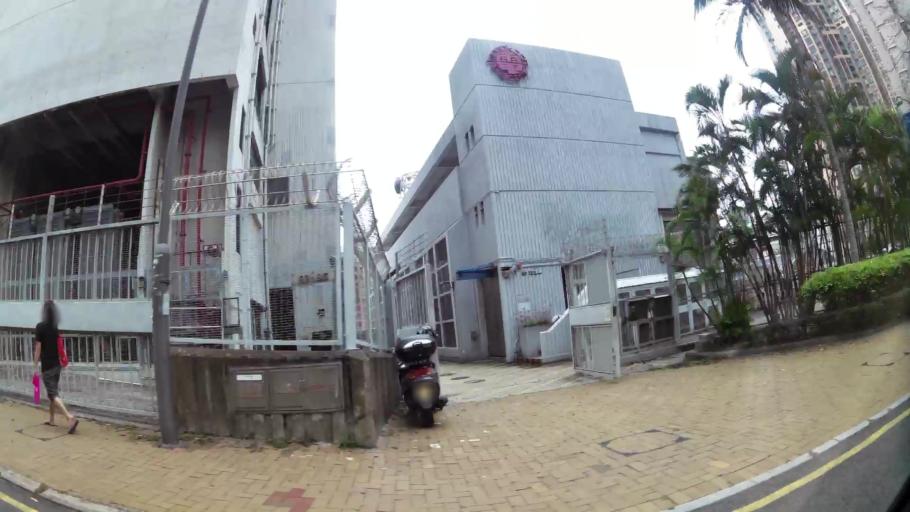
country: HK
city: Hong Kong
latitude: 22.2833
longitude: 114.1327
